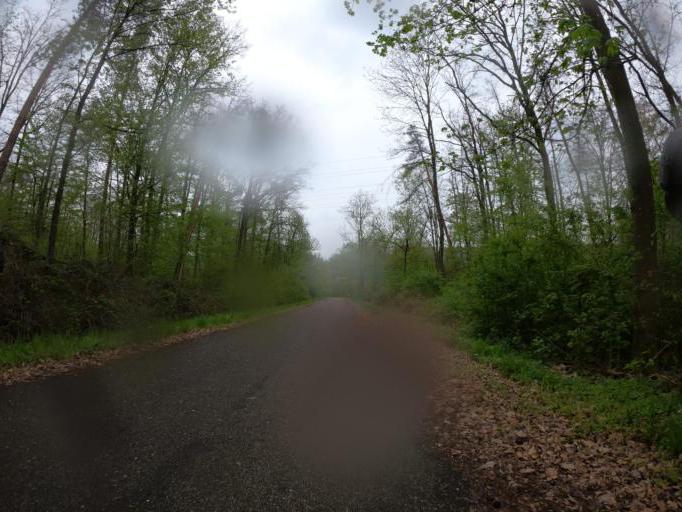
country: DE
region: Baden-Wuerttemberg
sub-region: Karlsruhe Region
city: Muhlacker
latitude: 48.9577
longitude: 8.8702
